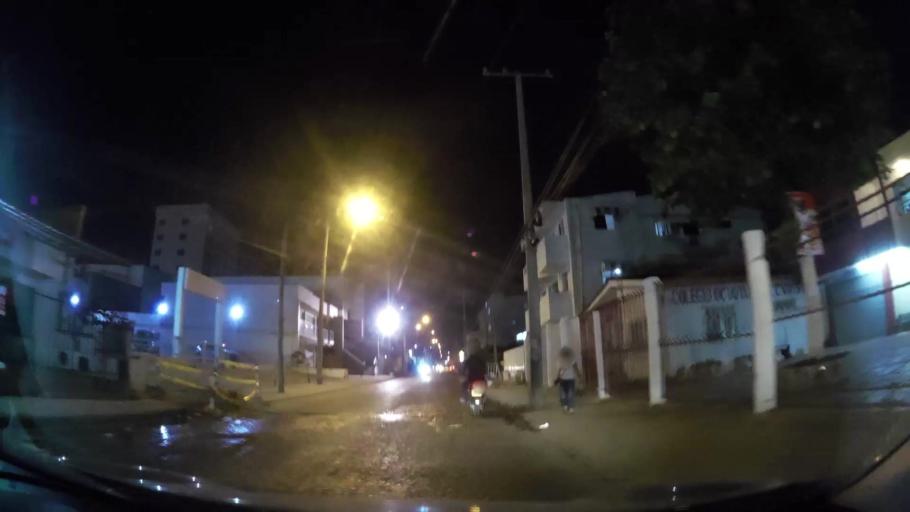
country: CO
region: Bolivar
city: Cartagena
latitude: 10.4081
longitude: -75.5146
